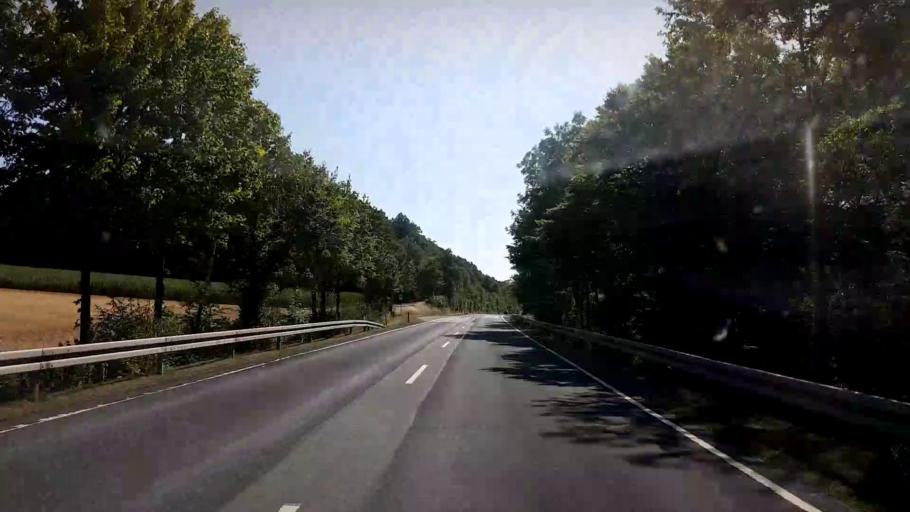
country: DE
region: Bavaria
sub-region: Upper Franconia
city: Grossheirath
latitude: 50.1498
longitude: 10.9184
